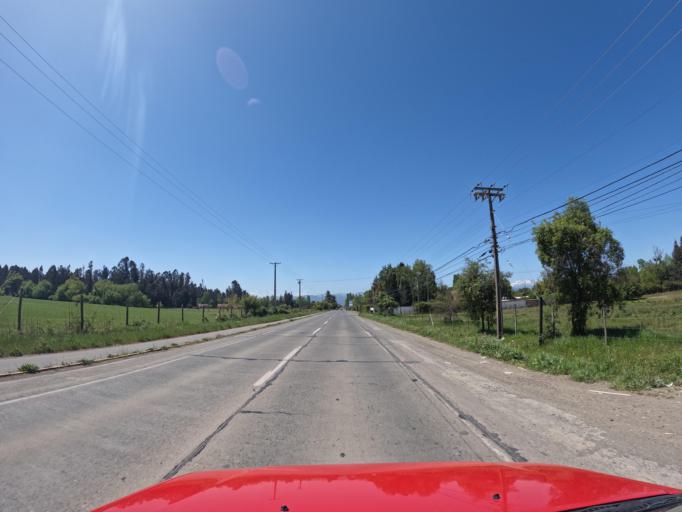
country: CL
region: Maule
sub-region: Provincia de Linares
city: Linares
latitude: -35.8346
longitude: -71.5463
